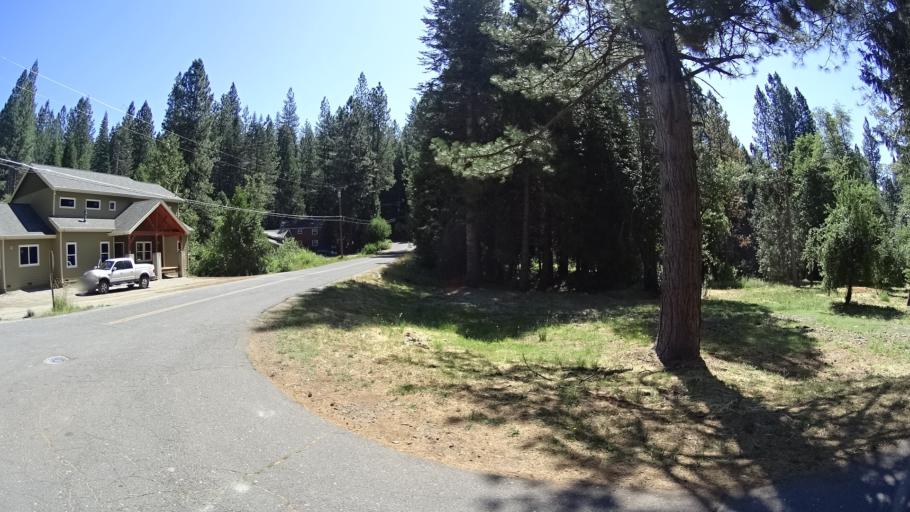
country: US
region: California
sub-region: Calaveras County
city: Arnold
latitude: 38.2375
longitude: -120.3775
